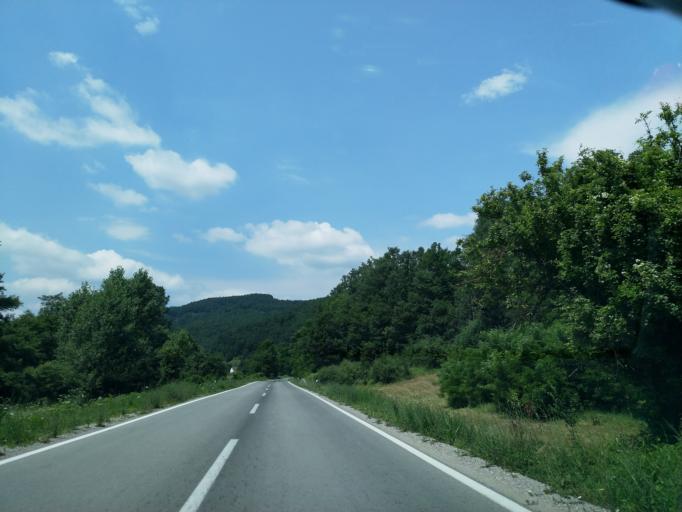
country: RS
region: Central Serbia
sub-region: Toplicki Okrug
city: Blace
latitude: 43.3283
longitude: 21.2199
